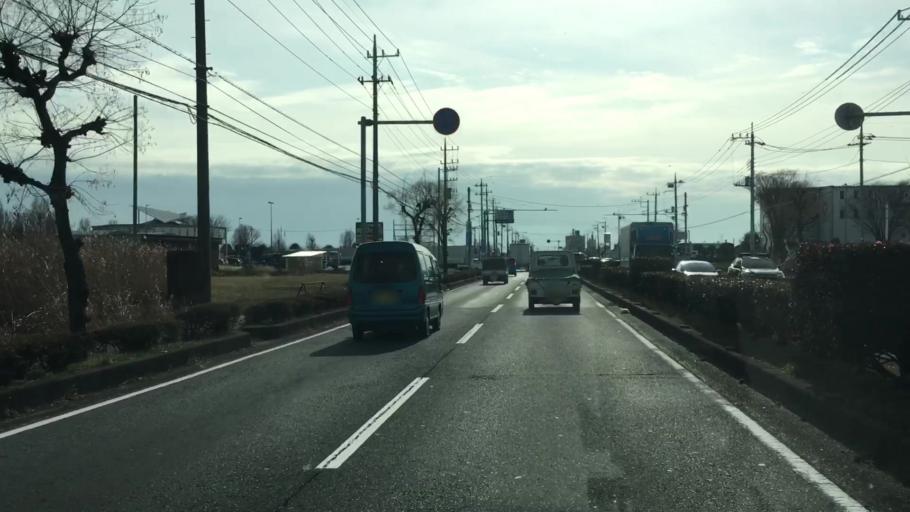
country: JP
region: Saitama
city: Menuma
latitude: 36.2167
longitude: 139.3684
